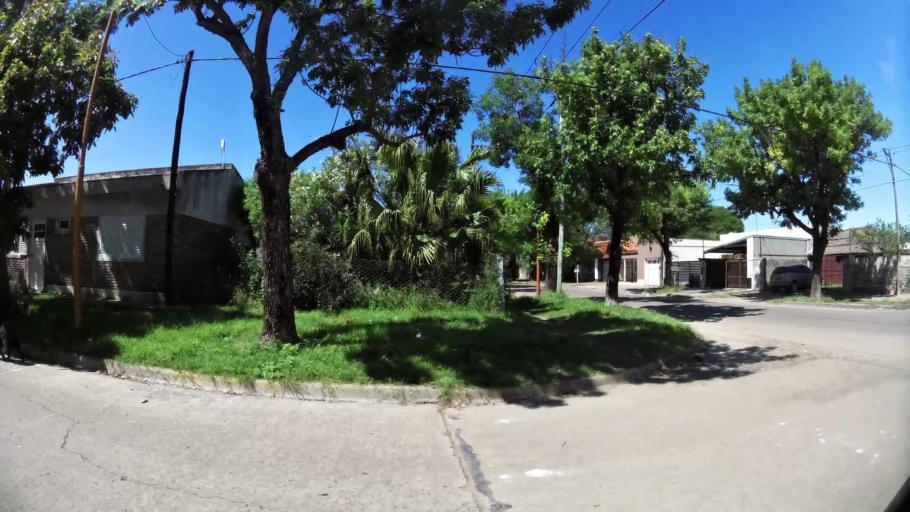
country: AR
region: Santa Fe
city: Esperanza
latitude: -31.4390
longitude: -60.9262
